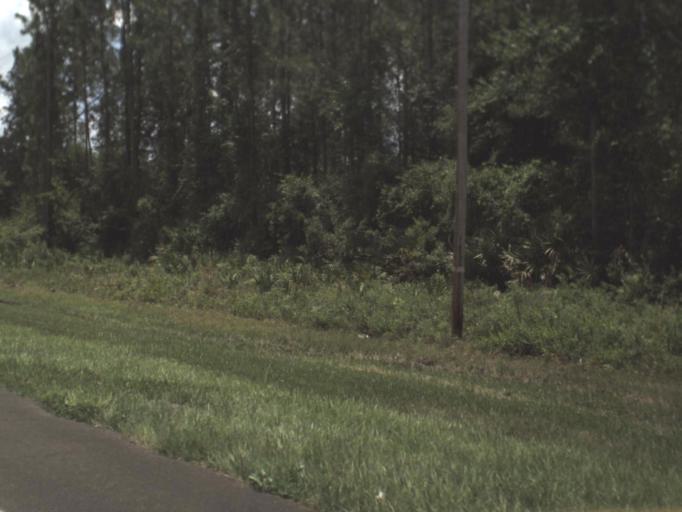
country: US
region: Florida
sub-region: Alachua County
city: Alachua
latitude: 29.7595
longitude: -82.3588
